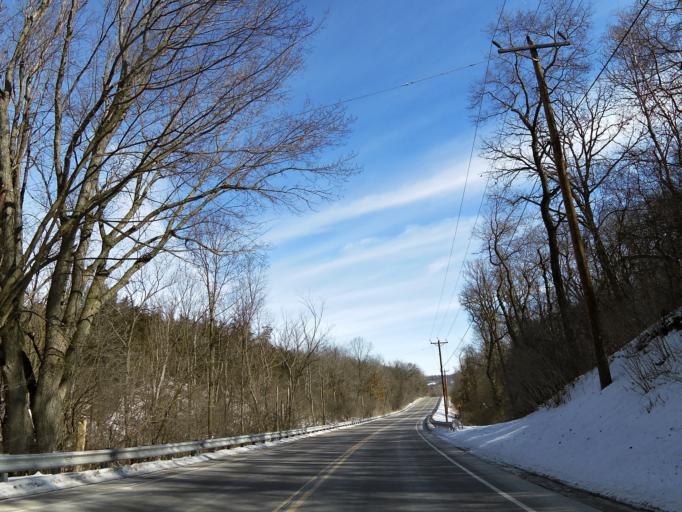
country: US
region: Minnesota
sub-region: Washington County
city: Afton
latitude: 44.8911
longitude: -92.8198
